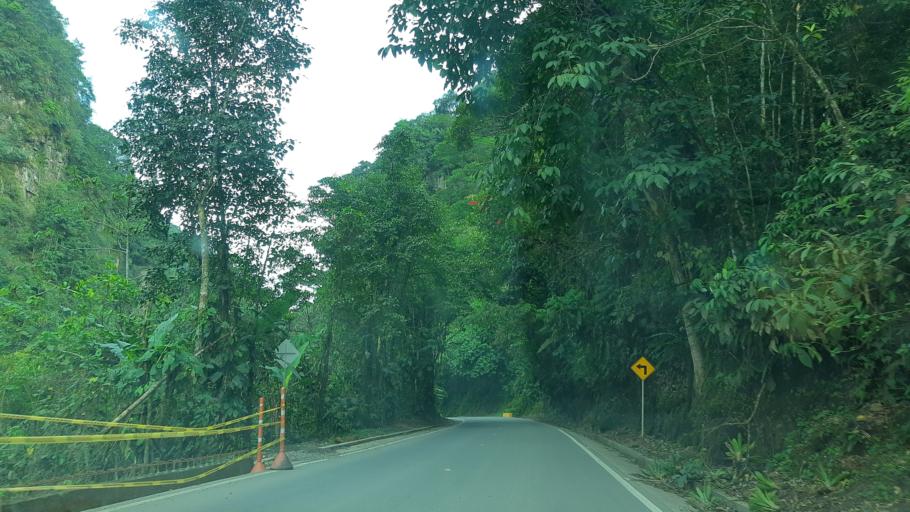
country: CO
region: Boyaca
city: Santa Maria
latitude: 4.8528
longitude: -73.2306
